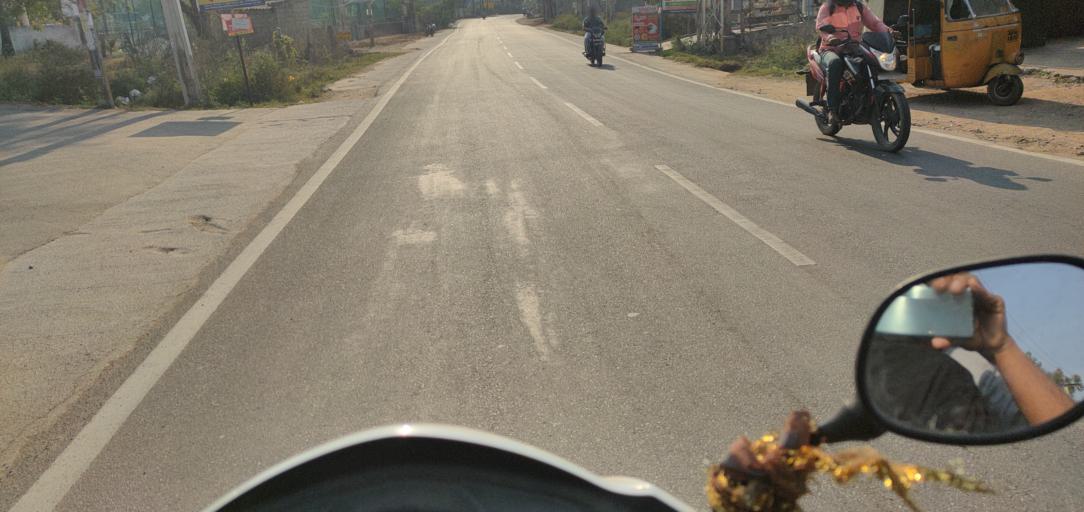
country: IN
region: Telangana
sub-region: Rangareddi
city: Lal Bahadur Nagar
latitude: 17.3375
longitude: 78.6182
